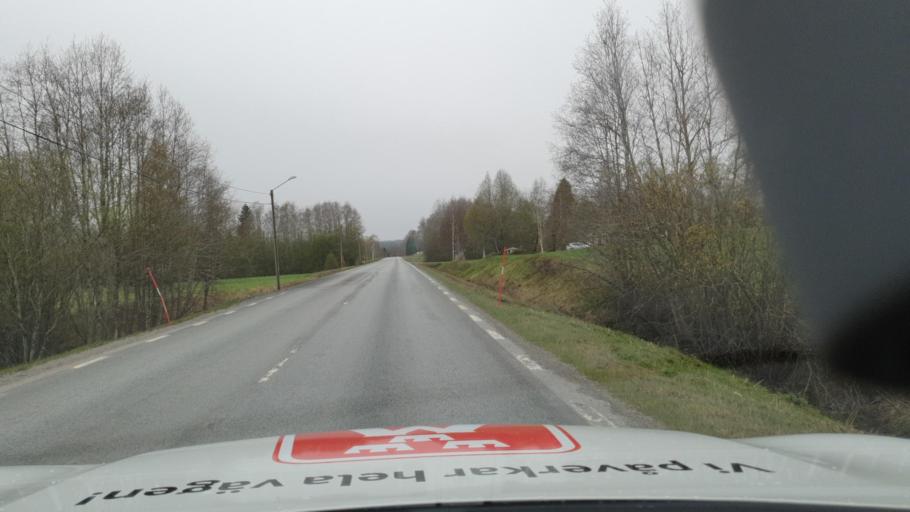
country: SE
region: Vaesterbotten
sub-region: Vannas Kommun
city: Vaennaes
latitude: 63.7735
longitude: 19.6796
